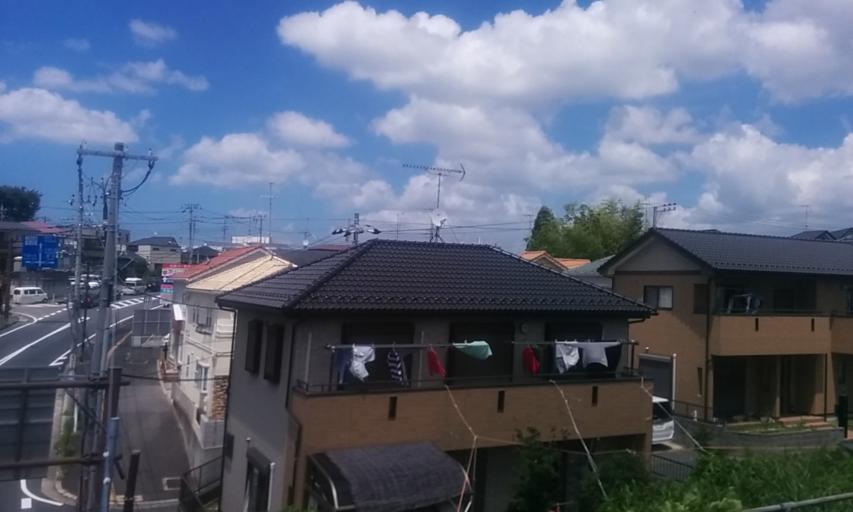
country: JP
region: Chiba
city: Chiba
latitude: 35.5649
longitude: 140.1747
